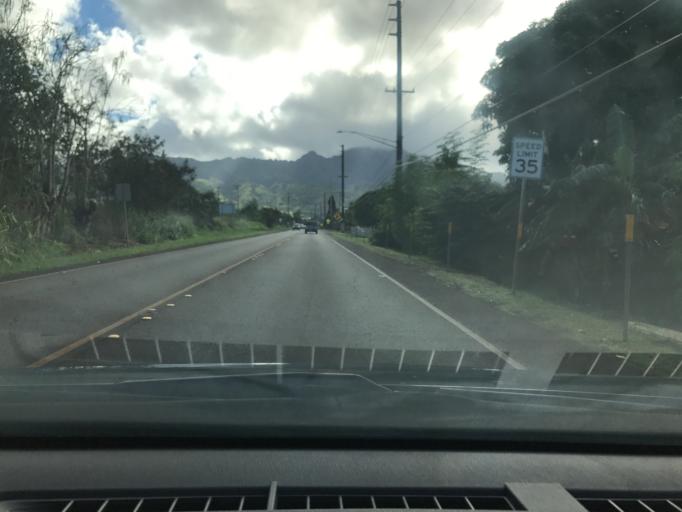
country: US
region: Hawaii
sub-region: Honolulu County
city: Hale'iwa
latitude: 21.5737
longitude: -158.1073
